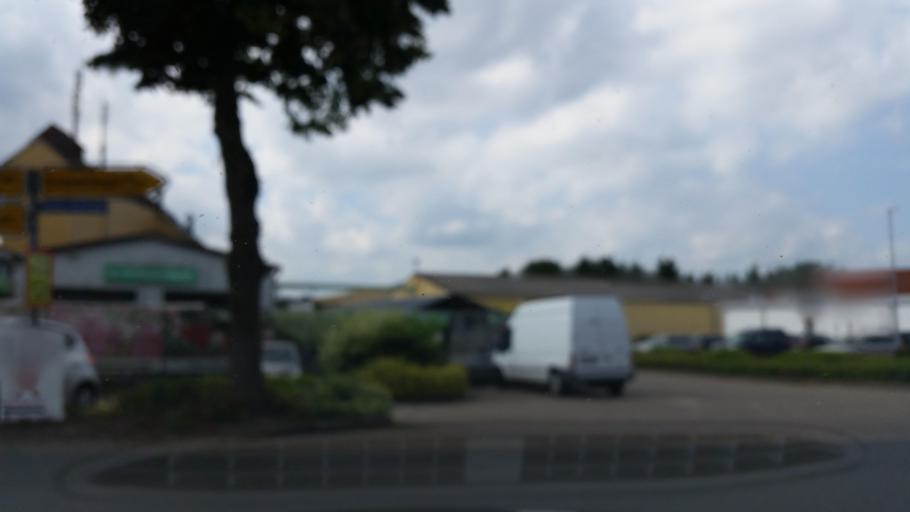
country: DE
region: Lower Saxony
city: Neuenkirchen
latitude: 53.0389
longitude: 9.7084
